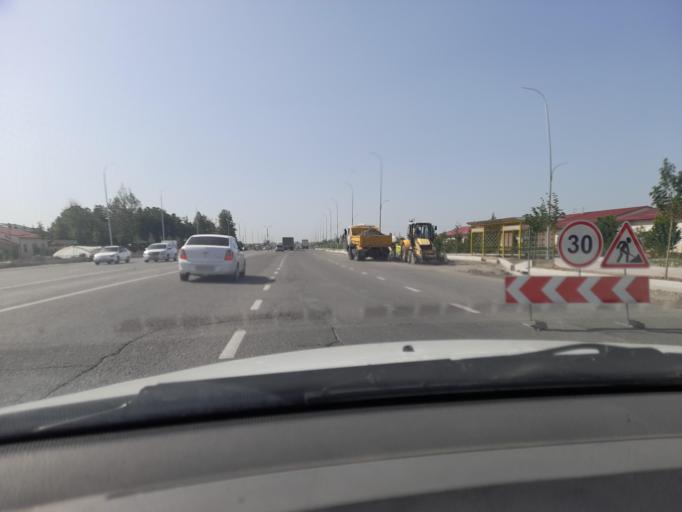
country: UZ
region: Samarqand
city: Daxbet
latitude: 39.7333
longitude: 66.9348
